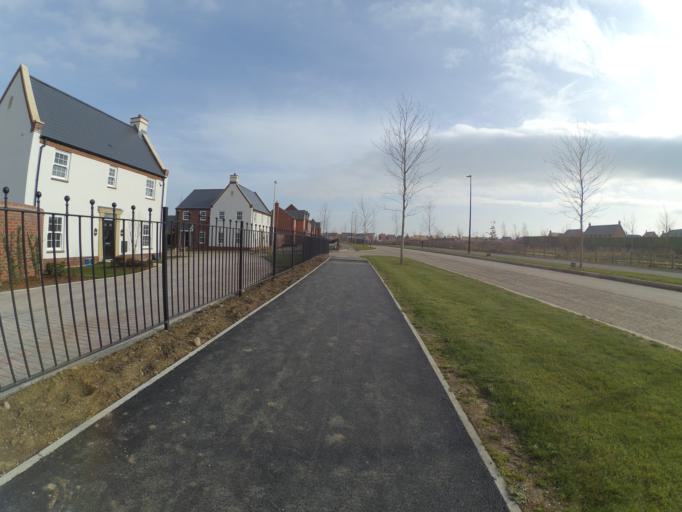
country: GB
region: England
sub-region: Warwickshire
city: Rugby
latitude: 52.3592
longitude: -1.1888
